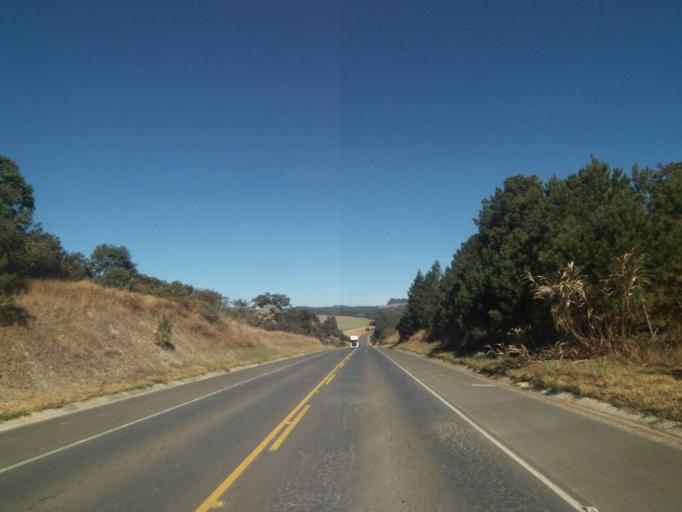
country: BR
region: Parana
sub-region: Tibagi
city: Tibagi
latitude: -24.5443
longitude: -50.4496
